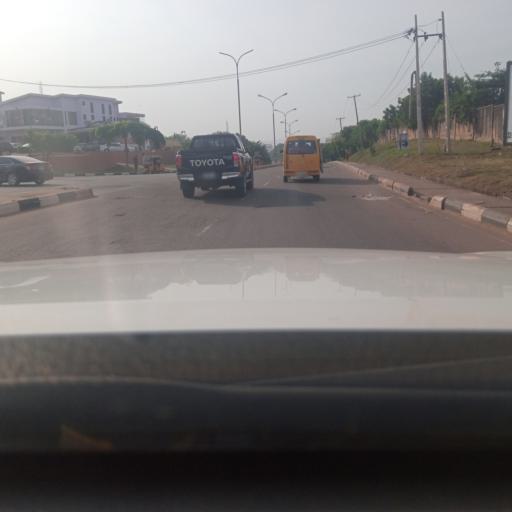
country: NG
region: Enugu
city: Enugu
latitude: 6.4392
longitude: 7.5165
